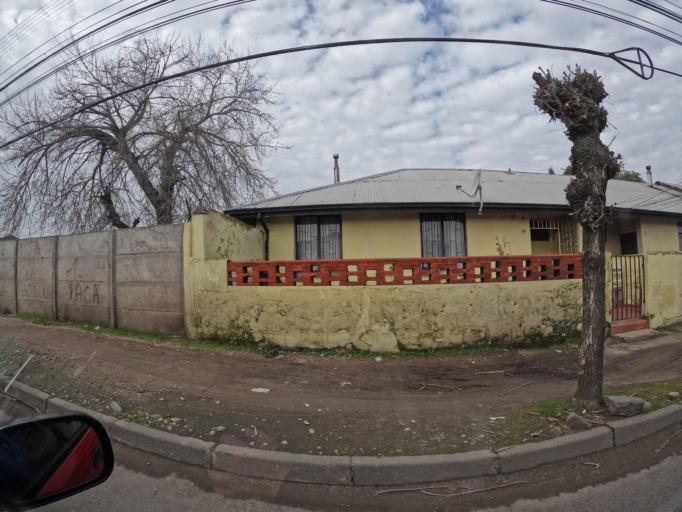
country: CL
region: Maule
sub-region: Provincia de Linares
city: Linares
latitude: -35.8398
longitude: -71.5949
